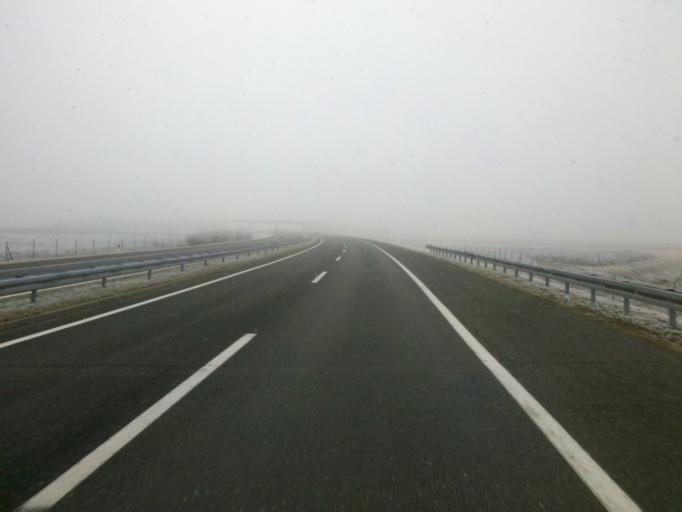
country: HR
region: Medimurska
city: Kursanec
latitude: 46.2667
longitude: 16.4072
